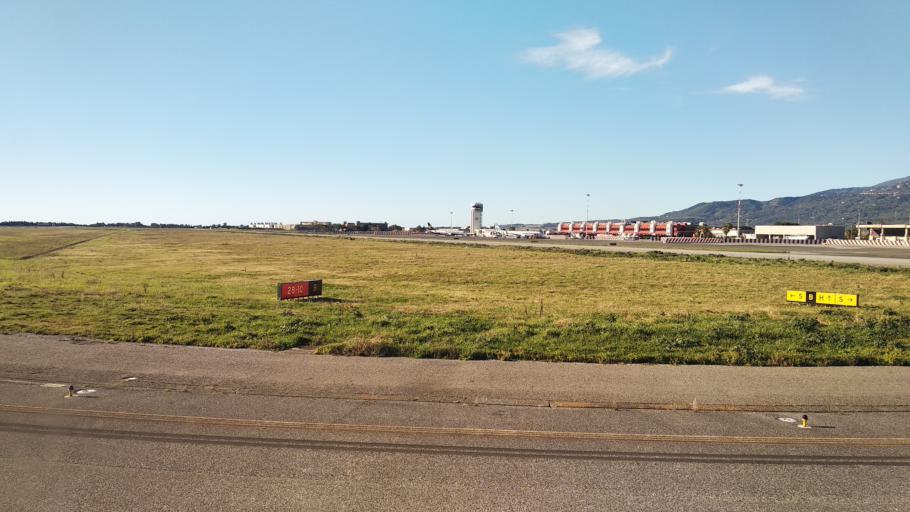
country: IT
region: Calabria
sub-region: Provincia di Catanzaro
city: Santa Eufemia Lamezia
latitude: 38.9057
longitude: 16.2501
